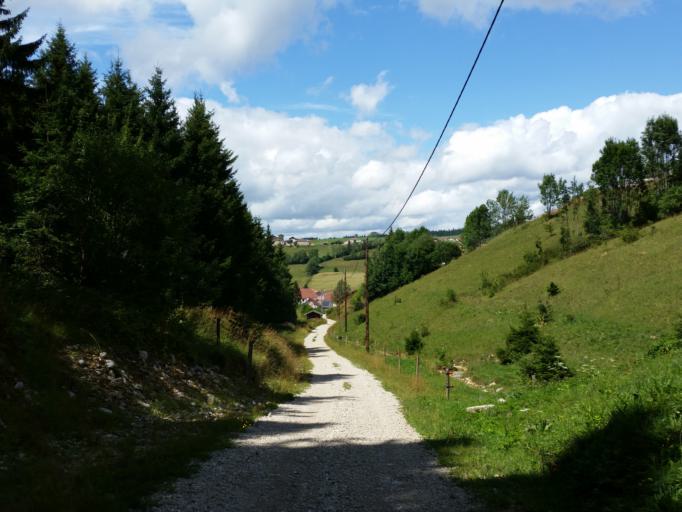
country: FR
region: Franche-Comte
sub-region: Departement du Doubs
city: Jougne
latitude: 46.7504
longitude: 6.3198
